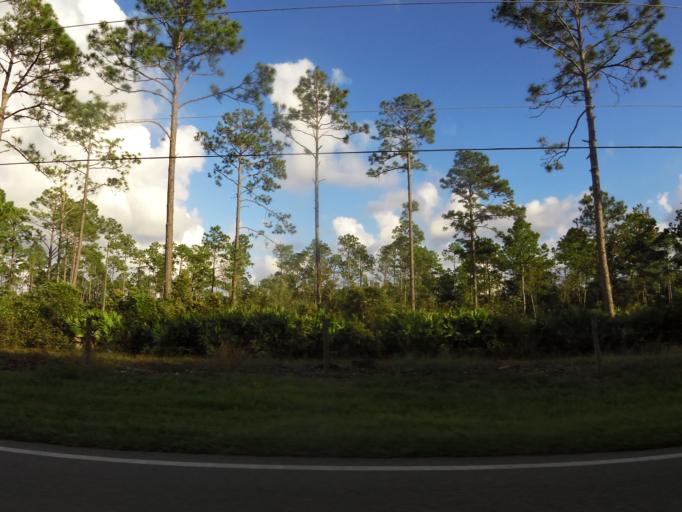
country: US
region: Florida
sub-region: Saint Johns County
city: Palm Valley
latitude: 30.1562
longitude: -81.3730
